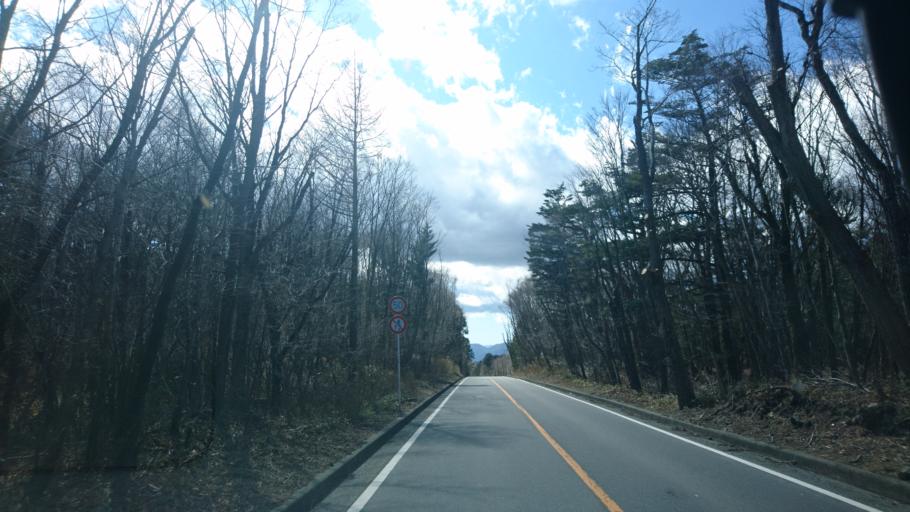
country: JP
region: Yamanashi
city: Fujikawaguchiko
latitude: 35.4353
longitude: 138.6385
